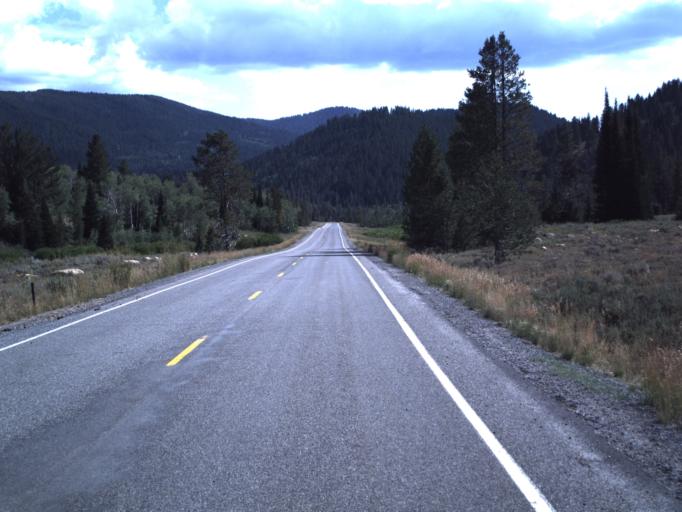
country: US
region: Utah
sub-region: Cache County
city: Richmond
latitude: 41.9724
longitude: -111.5320
